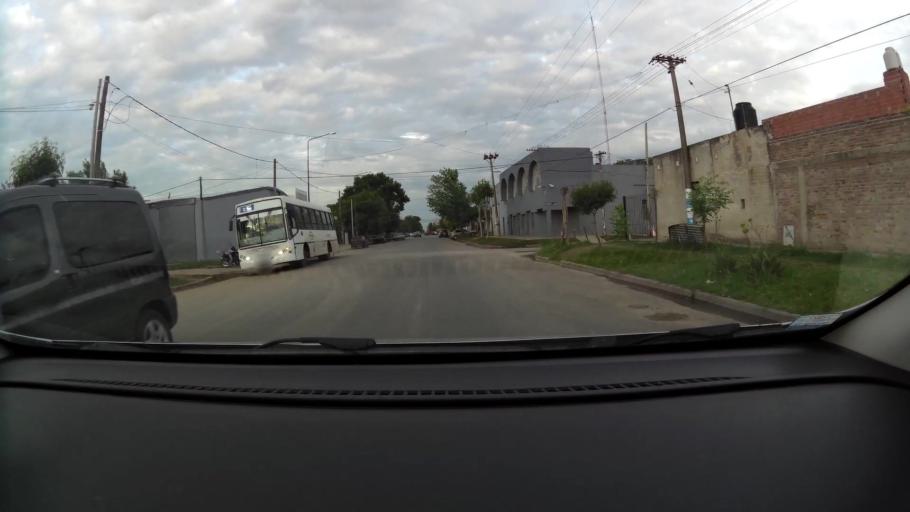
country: AR
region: Buenos Aires
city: San Nicolas de los Arroyos
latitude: -33.3204
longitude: -60.2430
